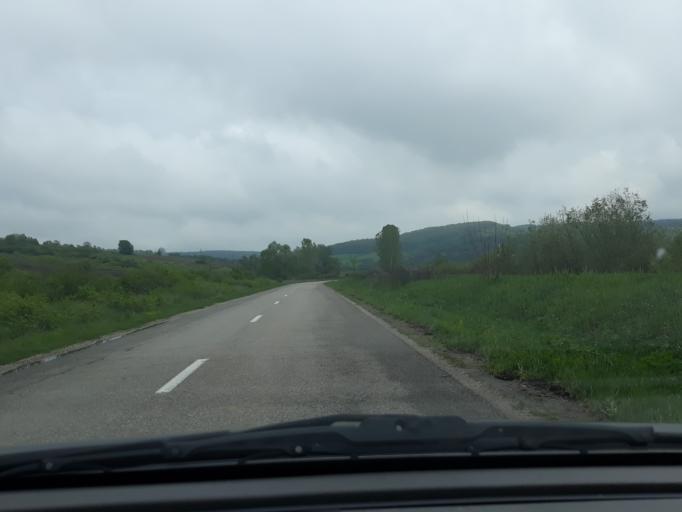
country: RO
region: Salaj
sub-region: Comuna Dobrin
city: Dobrin
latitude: 47.2953
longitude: 23.1173
